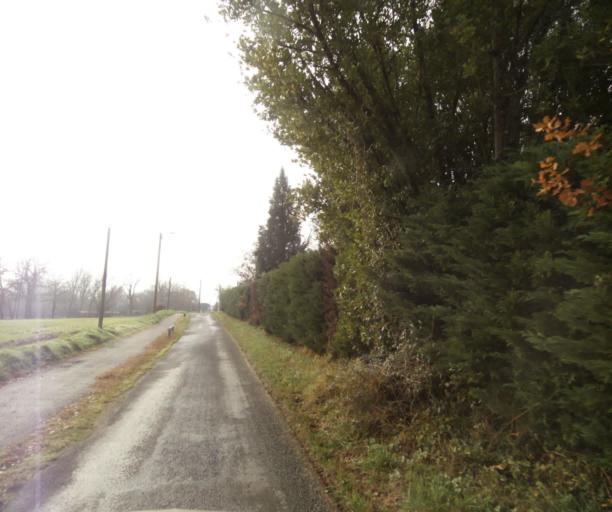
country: FR
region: Midi-Pyrenees
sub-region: Departement de la Haute-Garonne
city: Villemur-sur-Tarn
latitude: 43.8547
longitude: 1.4924
